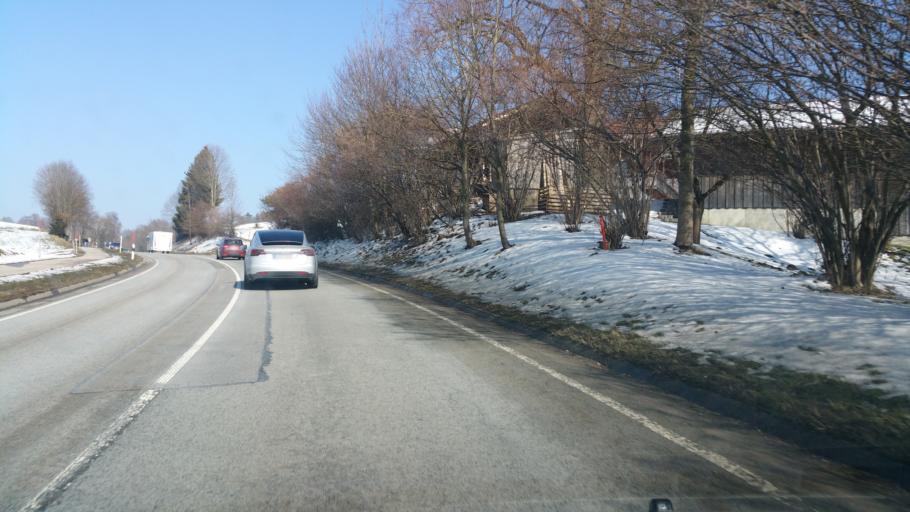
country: DE
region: Bavaria
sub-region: Upper Bavaria
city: Miesbach
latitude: 47.7991
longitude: 11.8493
